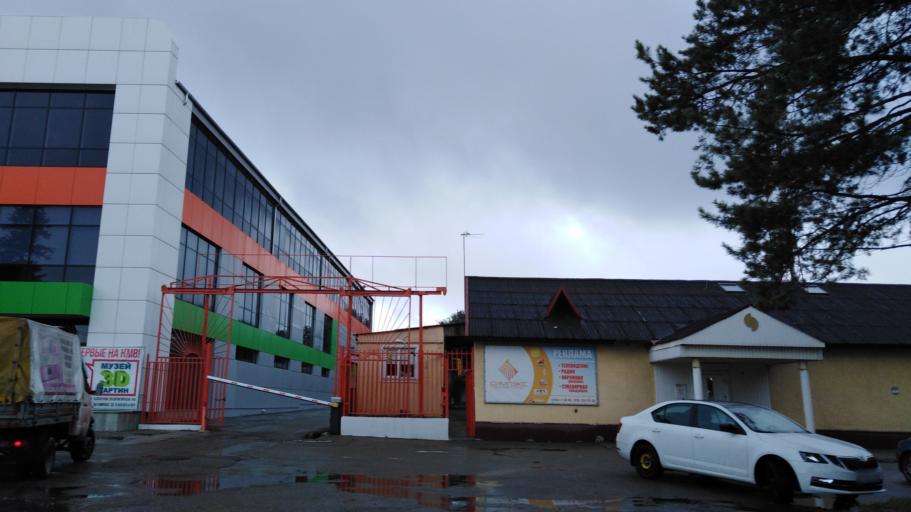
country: RU
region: Stavropol'skiy
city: Yessentukskaya
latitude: 44.0545
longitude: 42.9075
